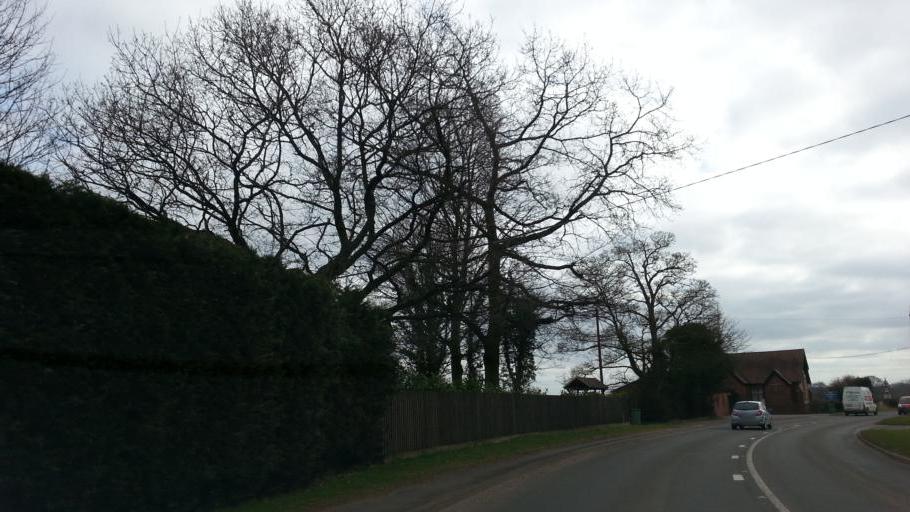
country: GB
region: England
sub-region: Staffordshire
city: Colwich
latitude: 52.8400
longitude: -2.0319
